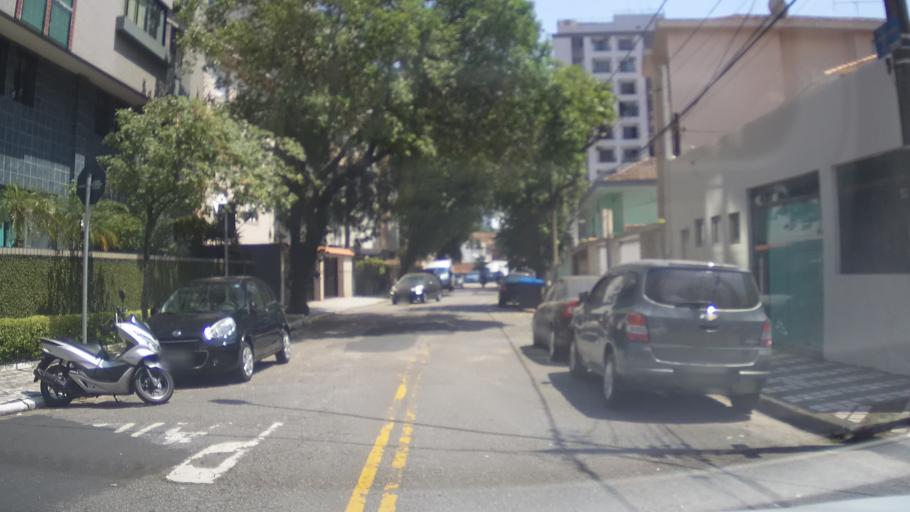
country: BR
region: Sao Paulo
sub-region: Santos
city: Santos
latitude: -23.9817
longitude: -46.3009
